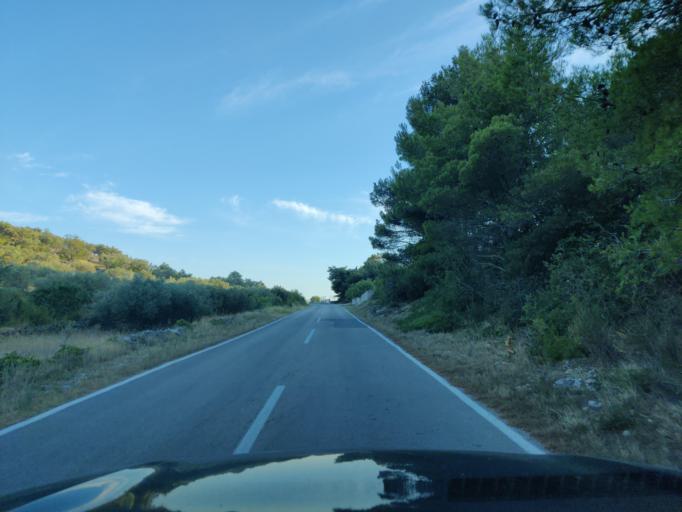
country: HR
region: Sibensko-Kniniska
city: Tribunj
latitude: 43.7890
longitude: 15.7280
